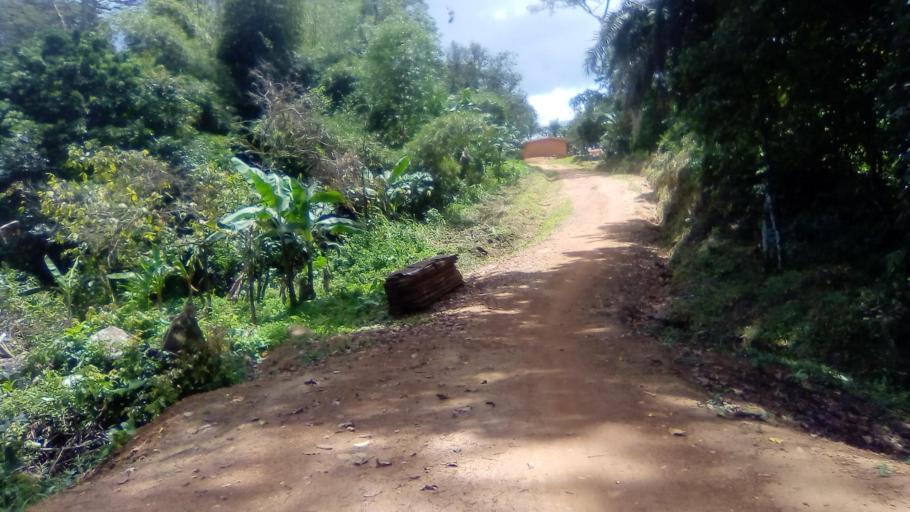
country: SL
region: Eastern Province
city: Giehun
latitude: 8.4974
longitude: -10.9080
